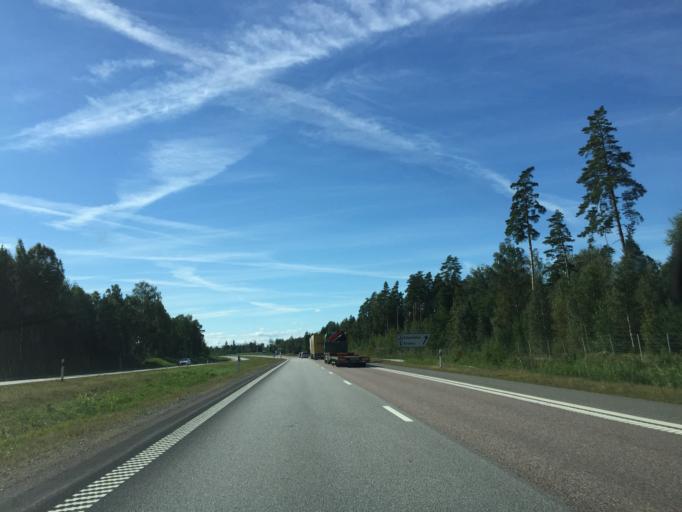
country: SE
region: OErebro
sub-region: Orebro Kommun
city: Odensbacken
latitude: 59.3164
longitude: 15.4500
